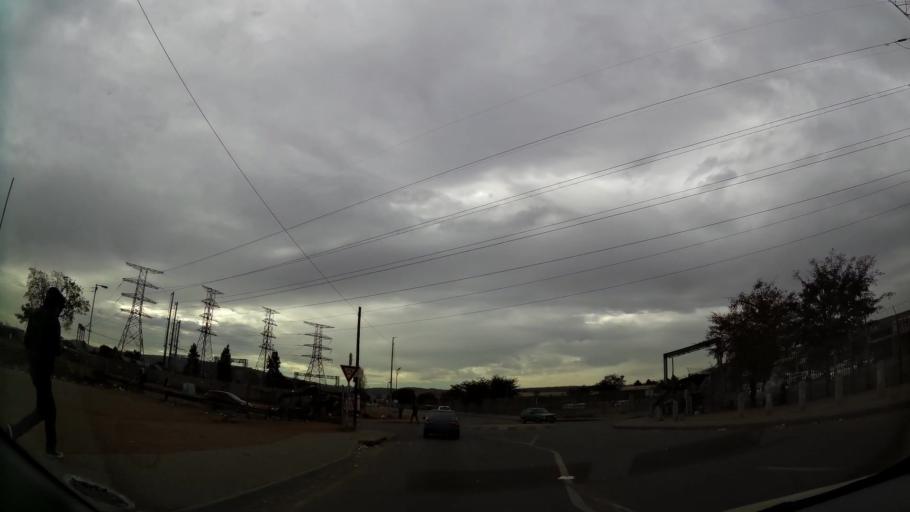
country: ZA
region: Gauteng
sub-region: City of Tshwane Metropolitan Municipality
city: Pretoria
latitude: -25.7156
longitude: 28.3309
